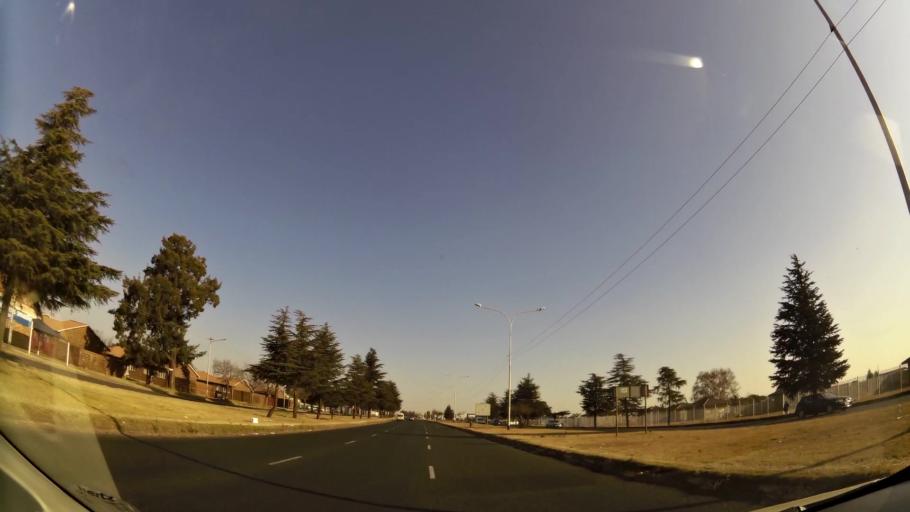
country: ZA
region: Gauteng
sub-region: West Rand District Municipality
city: Randfontein
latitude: -26.1976
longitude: 27.6990
